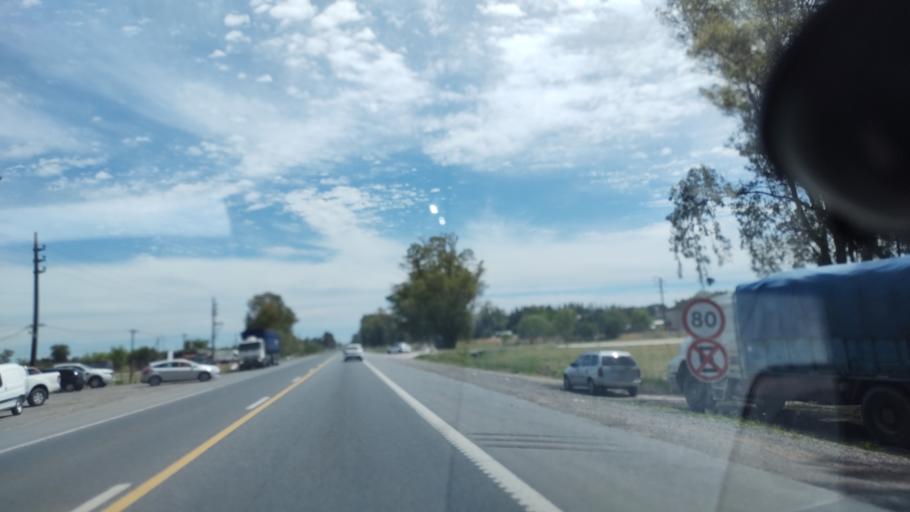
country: AR
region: Buenos Aires
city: Canuelas
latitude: -35.0307
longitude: -58.7502
